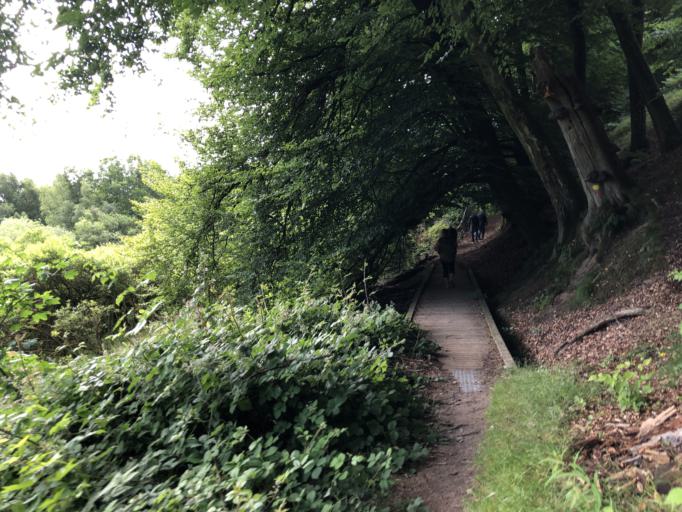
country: DK
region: Central Jutland
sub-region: Viborg Kommune
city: Viborg
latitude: 56.3709
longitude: 9.3250
